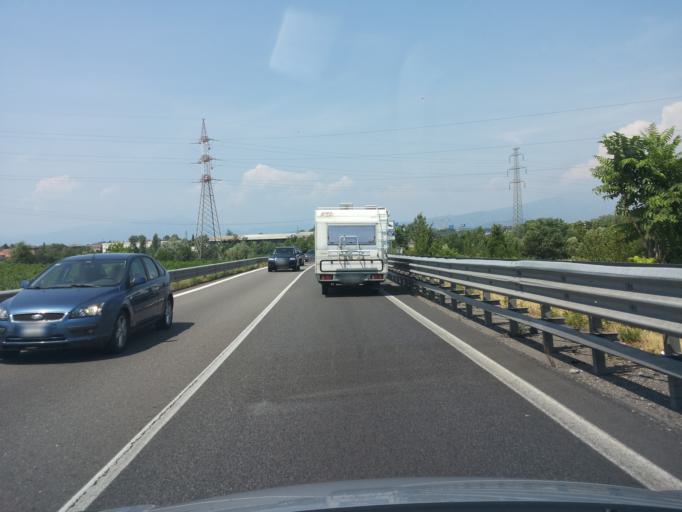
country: IT
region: Veneto
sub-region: Provincia di Verona
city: Cavalcaselle
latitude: 45.4321
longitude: 10.7416
